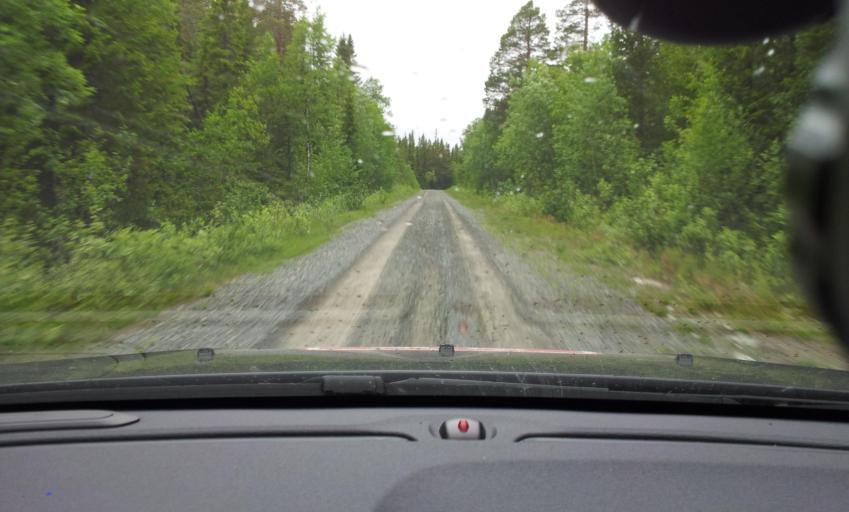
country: SE
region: Jaemtland
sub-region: Are Kommun
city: Jarpen
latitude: 63.1735
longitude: 13.5415
